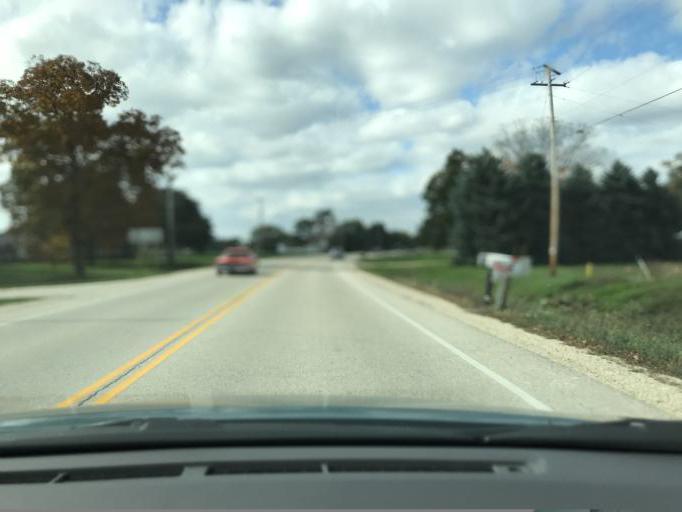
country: US
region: Wisconsin
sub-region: Racine County
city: Burlington
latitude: 42.6641
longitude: -88.2475
